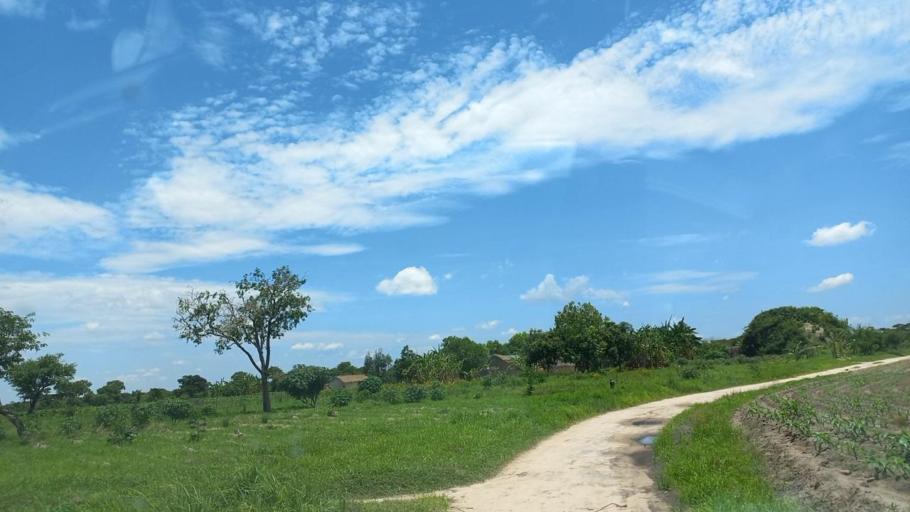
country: ZM
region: Copperbelt
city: Ndola
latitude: -12.8678
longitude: 28.4392
